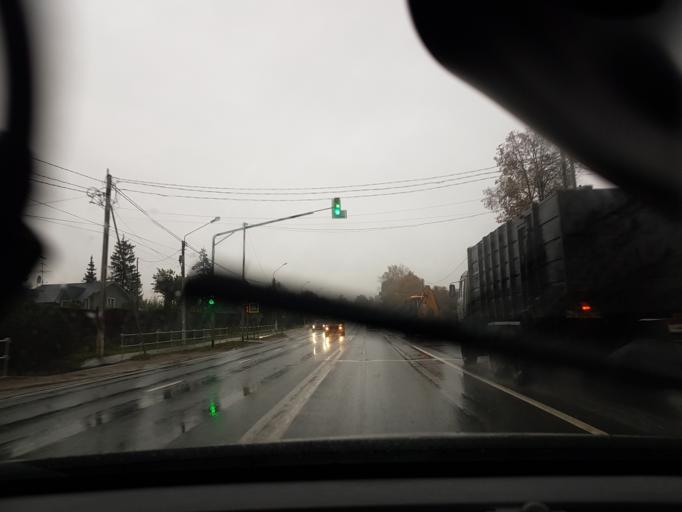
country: RU
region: Moskovskaya
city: Istra
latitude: 55.9079
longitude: 36.8809
